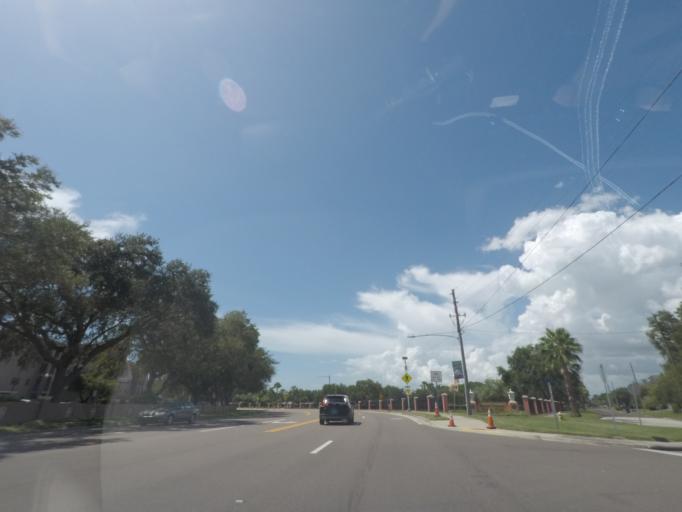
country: US
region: Florida
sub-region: Pinellas County
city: Gulfport
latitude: 27.7535
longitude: -82.7182
